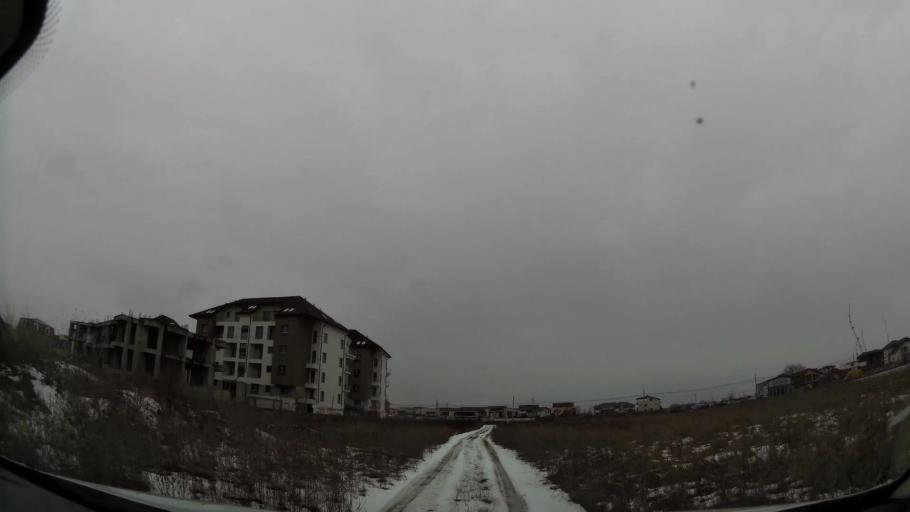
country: RO
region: Ilfov
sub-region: Comuna Otopeni
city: Otopeni
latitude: 44.5535
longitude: 26.0981
